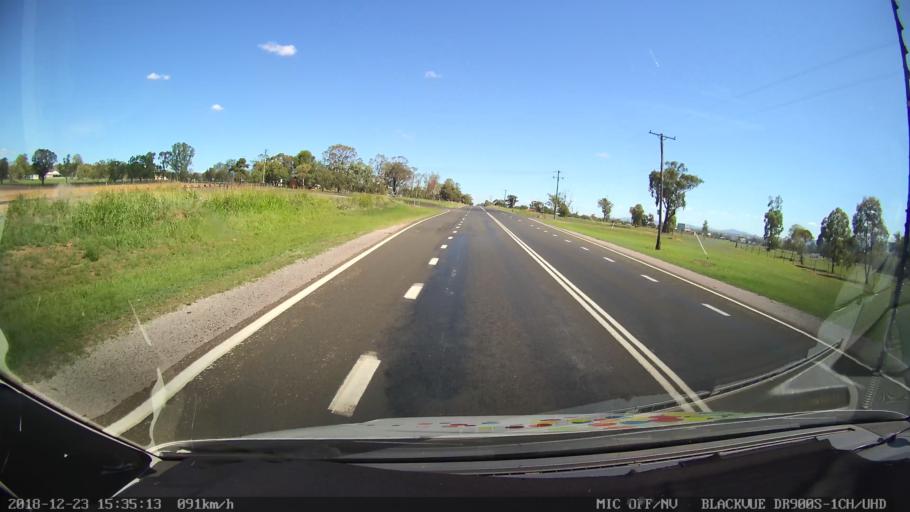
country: AU
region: New South Wales
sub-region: Tamworth Municipality
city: Tamworth
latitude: -31.0243
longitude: 150.8816
